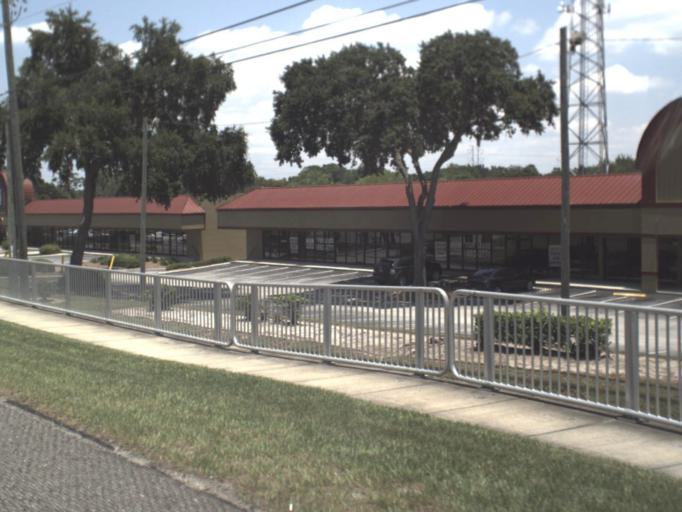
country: US
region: Florida
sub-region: Pinellas County
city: Saint George
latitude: 28.0532
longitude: -82.7386
